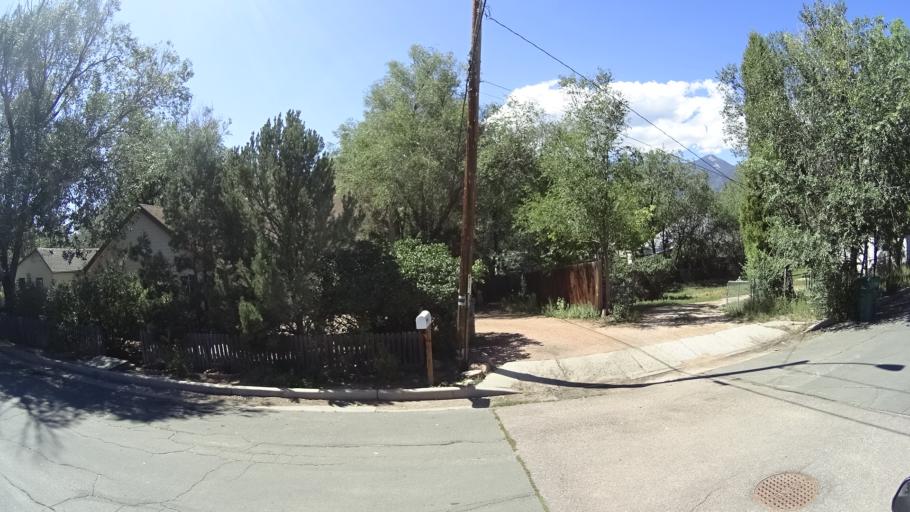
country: US
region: Colorado
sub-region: El Paso County
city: Colorado Springs
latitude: 38.8508
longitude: -104.8558
